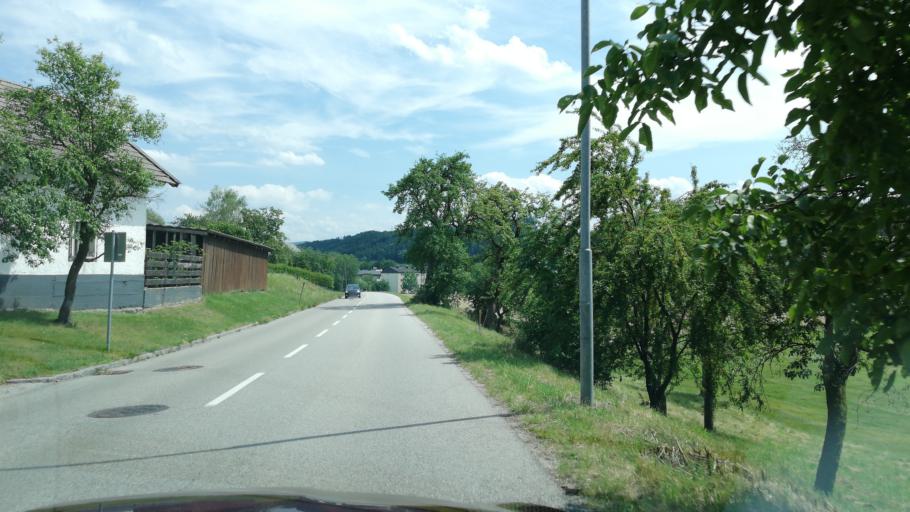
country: AT
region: Upper Austria
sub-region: Politischer Bezirk Vocklabruck
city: Vocklabruck
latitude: 47.9999
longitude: 13.6339
